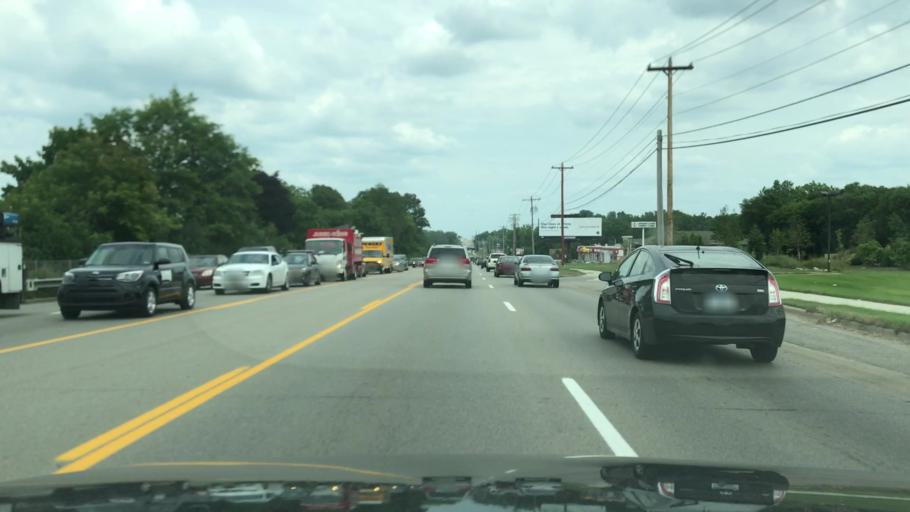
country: US
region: Michigan
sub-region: Kent County
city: East Grand Rapids
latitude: 42.9126
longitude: -85.6257
